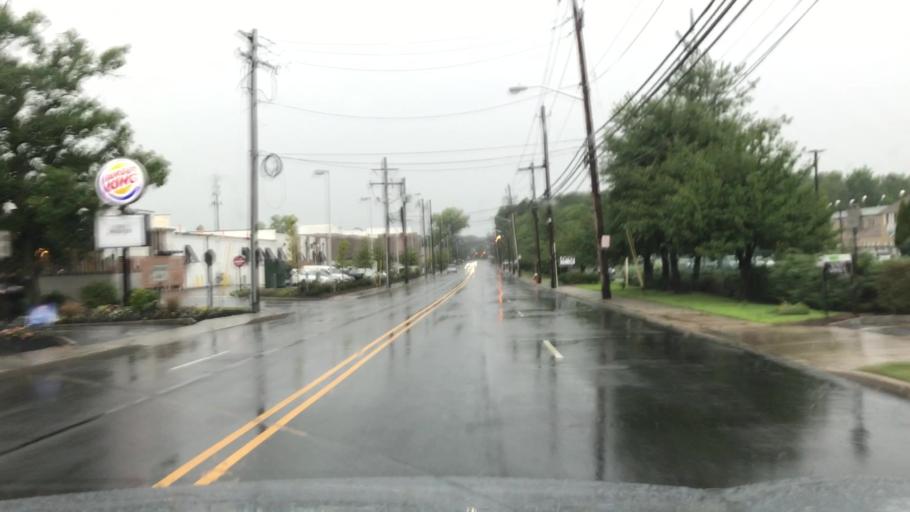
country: US
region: New Jersey
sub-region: Bergen County
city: Closter
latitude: 40.9701
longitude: -73.9541
